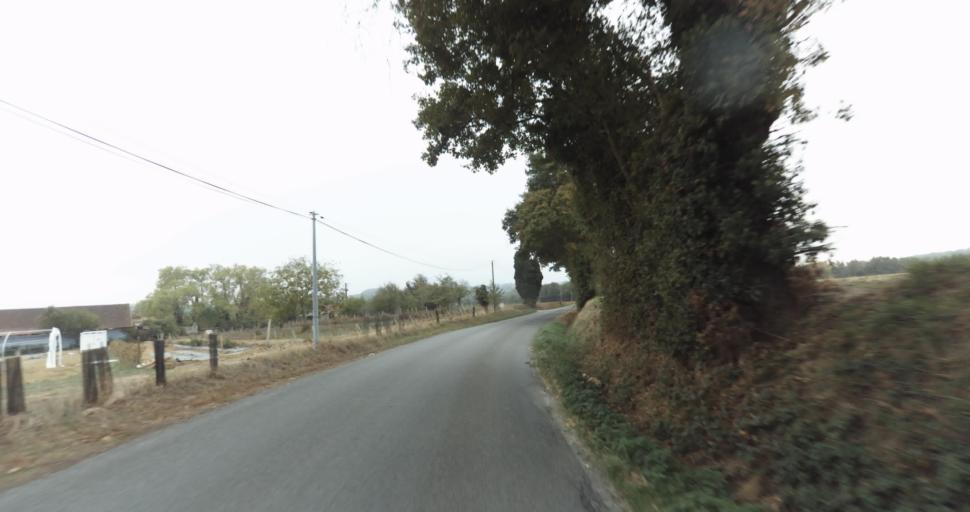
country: FR
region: Midi-Pyrenees
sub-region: Departement du Gers
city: Preignan
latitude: 43.6932
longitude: 0.5913
